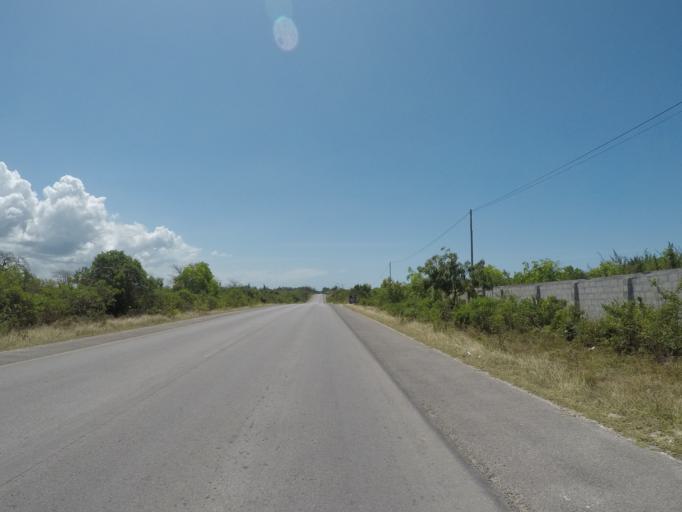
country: TZ
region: Zanzibar Central/South
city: Nganane
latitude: -6.2936
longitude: 39.5375
